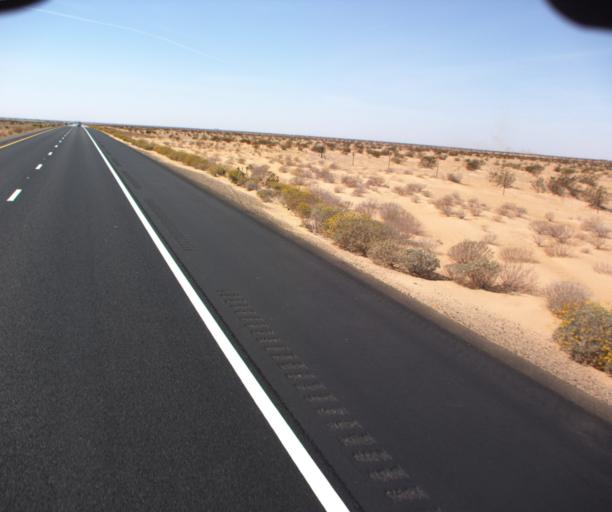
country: US
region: Arizona
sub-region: Yuma County
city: Somerton
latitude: 32.4954
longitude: -114.5869
